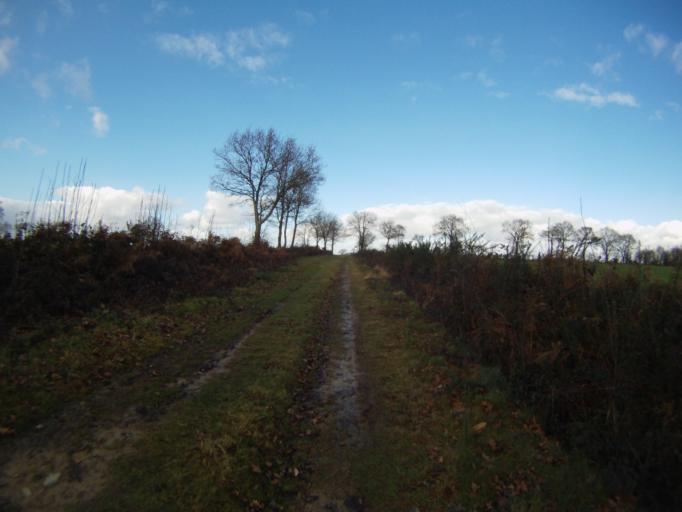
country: FR
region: Brittany
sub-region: Departement d'Ille-et-Vilaine
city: Chanteloup
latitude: 47.9351
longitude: -1.6270
